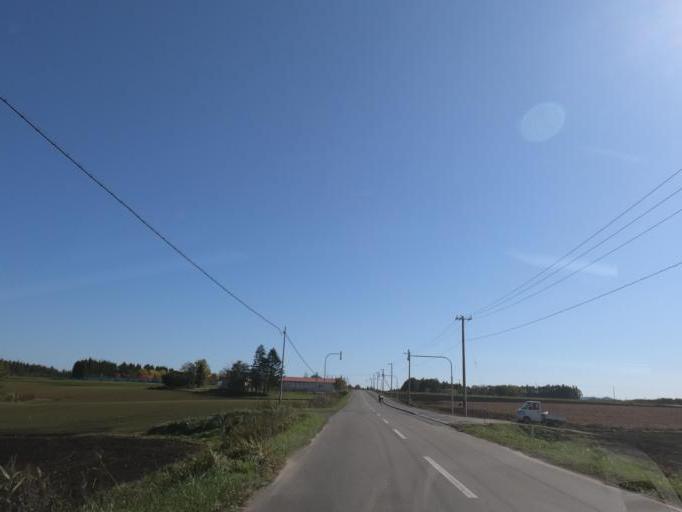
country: JP
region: Hokkaido
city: Obihiro
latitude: 42.8060
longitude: 143.2577
